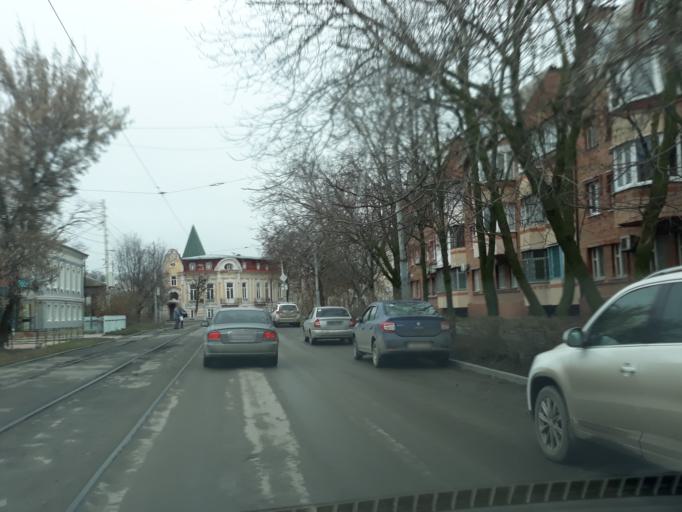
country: RU
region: Rostov
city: Taganrog
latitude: 47.2103
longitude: 38.9321
